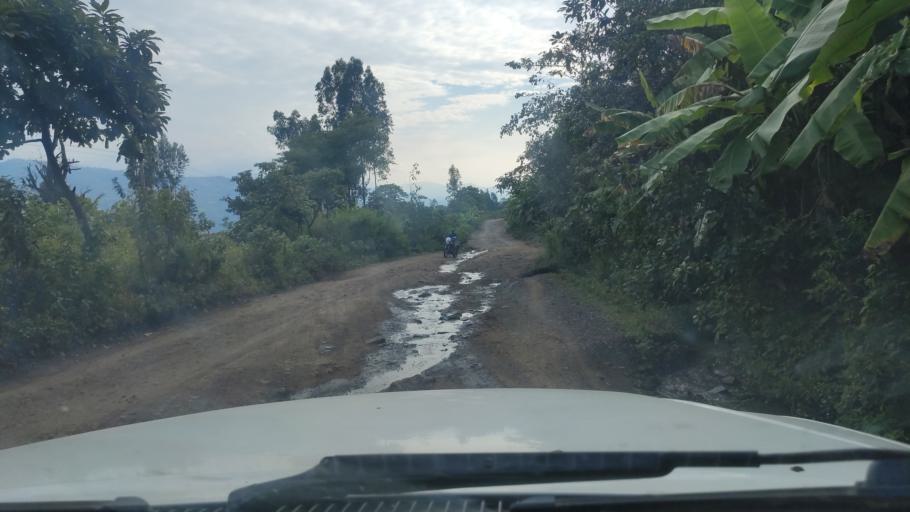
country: ET
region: Southern Nations, Nationalities, and People's Region
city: Arba Minch'
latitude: 6.4451
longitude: 37.3950
